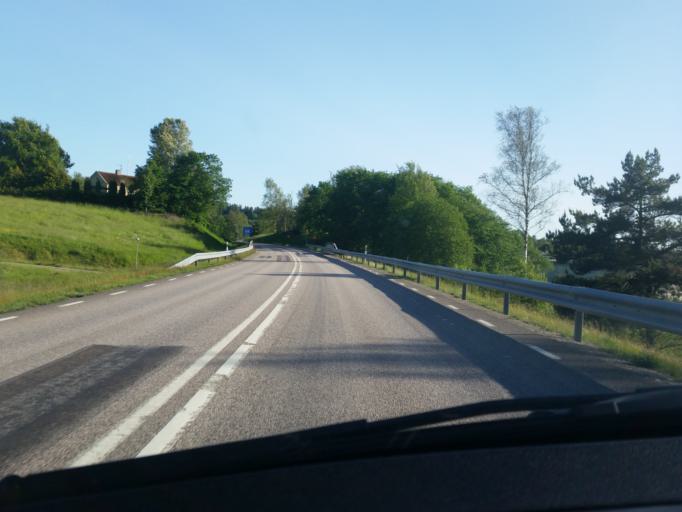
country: SE
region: Vaestra Goetaland
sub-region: Fargelanda Kommun
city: Faergelanda
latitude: 58.5734
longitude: 12.0056
